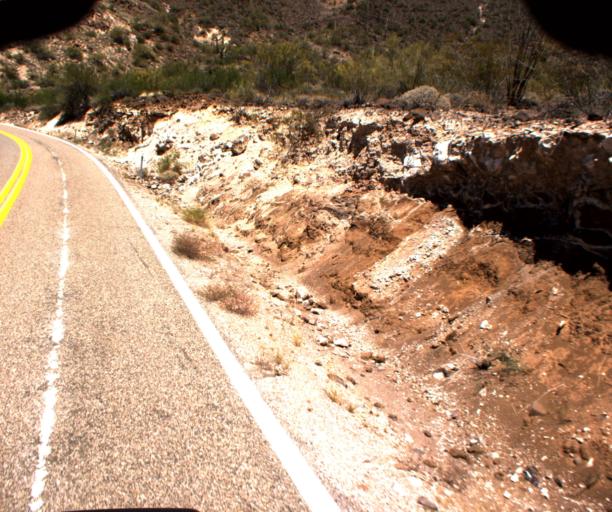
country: US
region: Arizona
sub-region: Yavapai County
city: Bagdad
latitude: 34.5041
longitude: -113.0686
